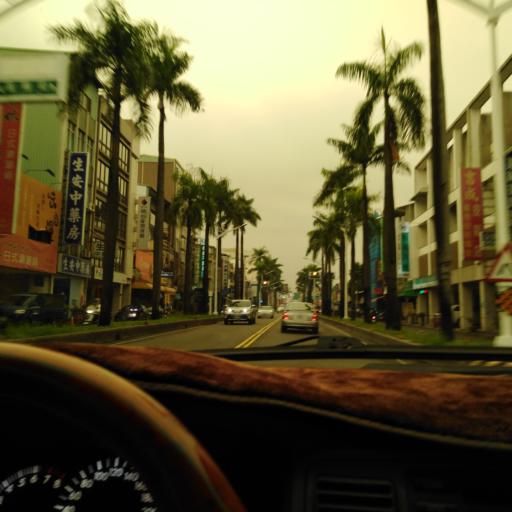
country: TW
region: Taiwan
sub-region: Pingtung
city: Pingtung
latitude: 22.6797
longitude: 120.4913
